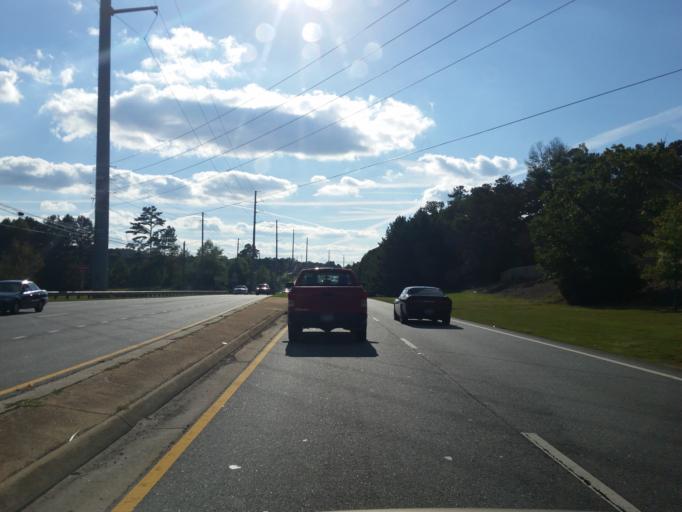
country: US
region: Georgia
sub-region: Cobb County
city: Powder Springs
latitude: 33.9434
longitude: -84.6953
